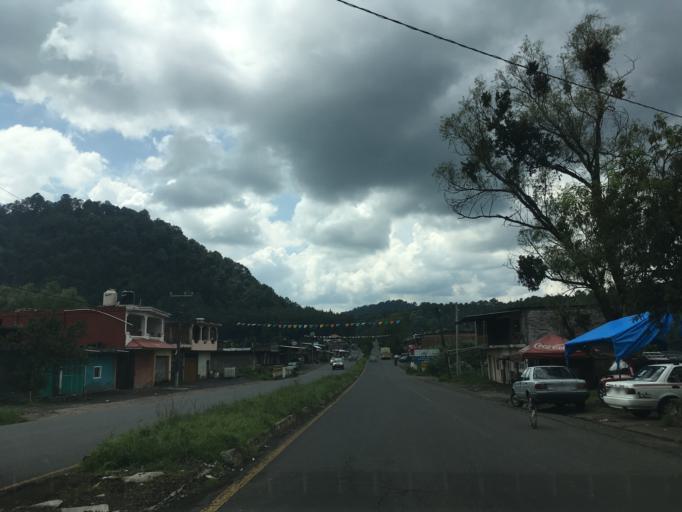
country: MX
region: Michoacan
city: Capacuaro
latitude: 19.5237
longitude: -102.1065
